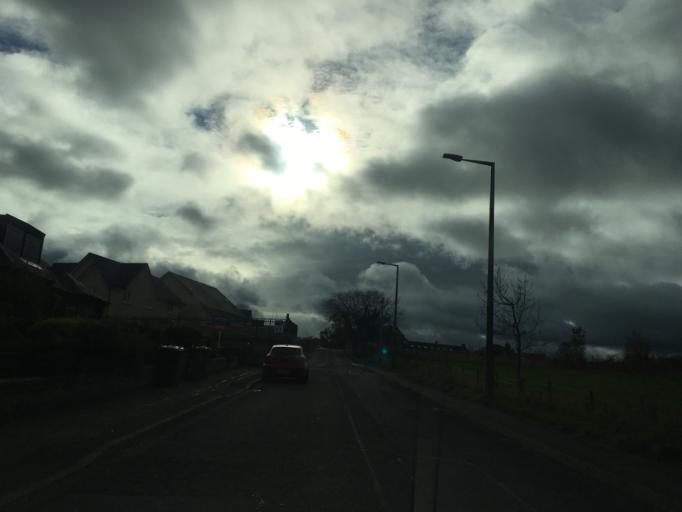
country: GB
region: Scotland
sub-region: Midlothian
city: Loanhead
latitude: 55.9109
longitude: -3.1686
